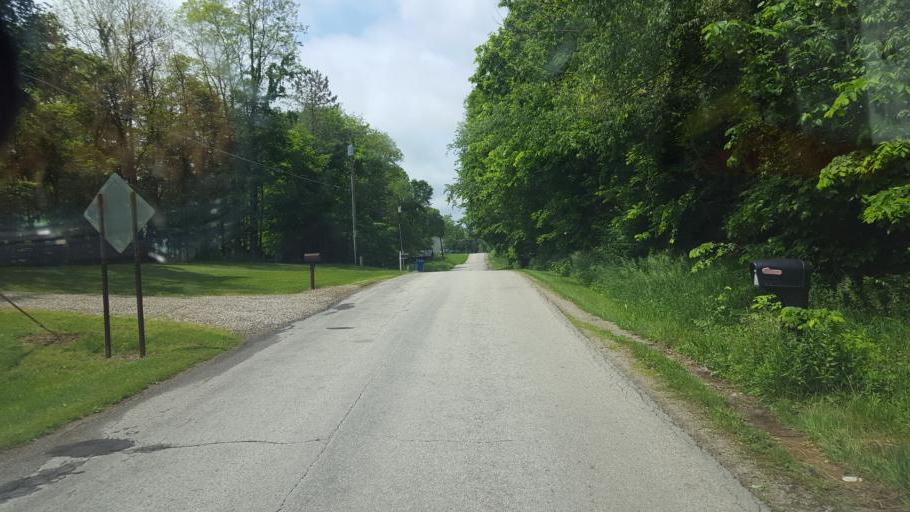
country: US
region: Ohio
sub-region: Delaware County
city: Ashley
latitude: 40.4050
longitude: -82.8674
